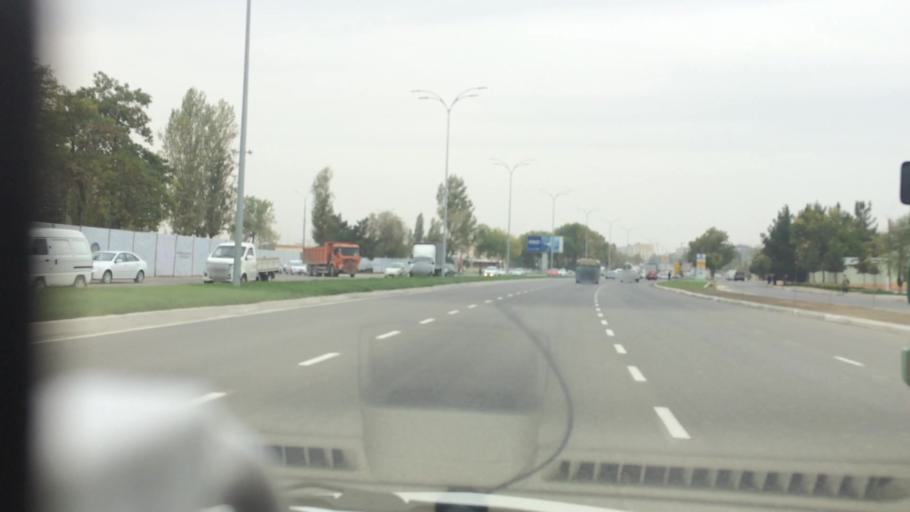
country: UZ
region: Toshkent
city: Salor
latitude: 41.3006
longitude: 69.3461
